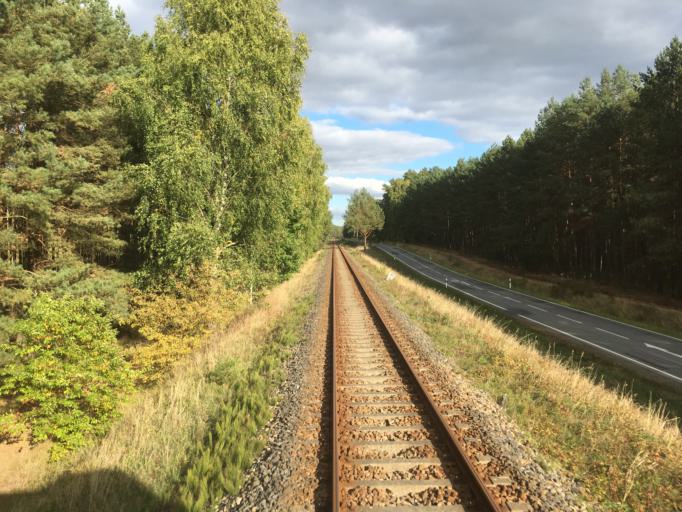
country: DE
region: Mecklenburg-Vorpommern
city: Malchow
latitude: 53.5311
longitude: 12.4843
